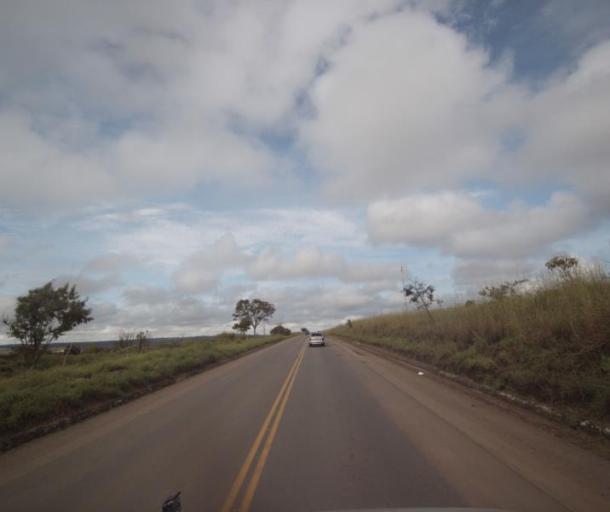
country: BR
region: Goias
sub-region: Pirenopolis
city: Pirenopolis
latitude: -15.7643
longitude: -48.7580
